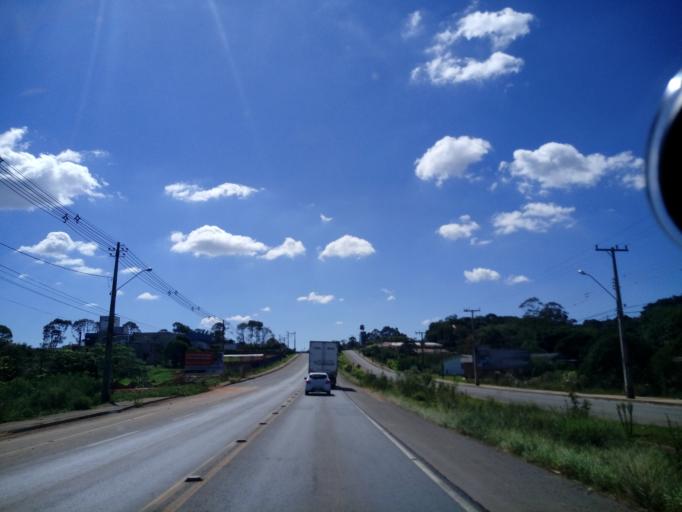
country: BR
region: Santa Catarina
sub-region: Chapeco
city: Chapeco
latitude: -27.1495
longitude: -52.6211
